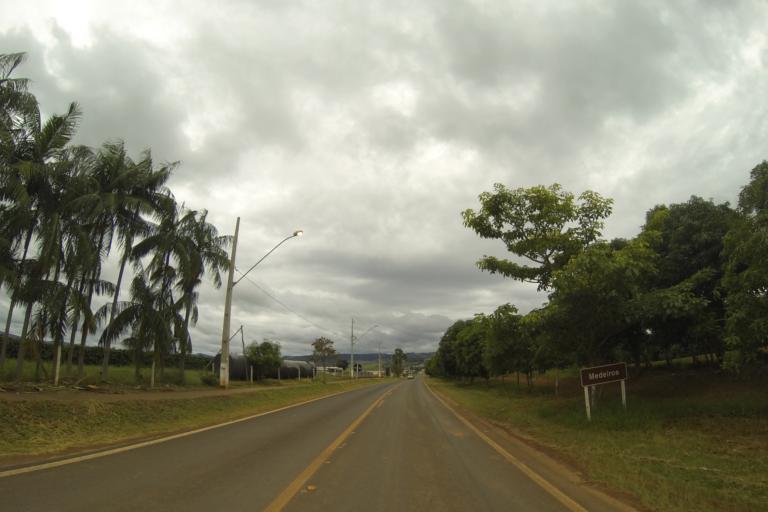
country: BR
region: Minas Gerais
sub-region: Bambui
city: Bambui
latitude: -20.0046
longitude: -46.2092
